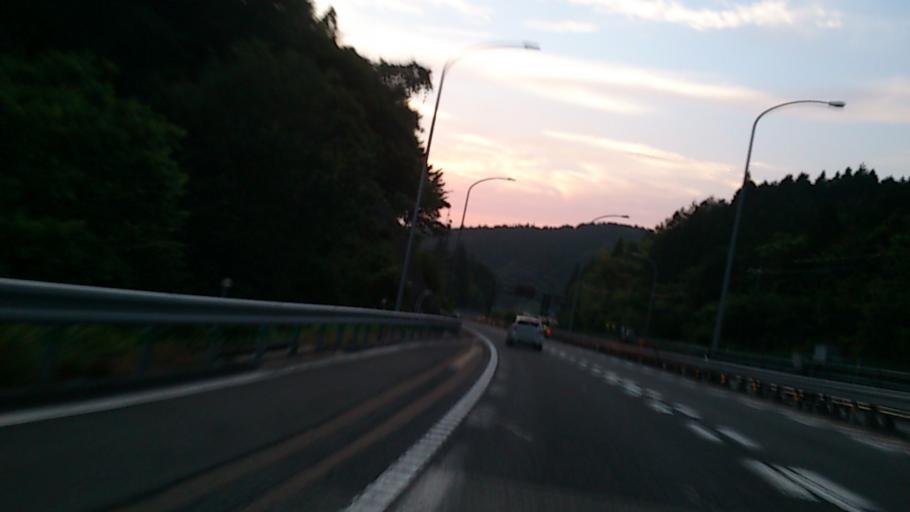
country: JP
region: Gifu
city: Nakatsugawa
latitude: 35.5084
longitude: 137.5885
